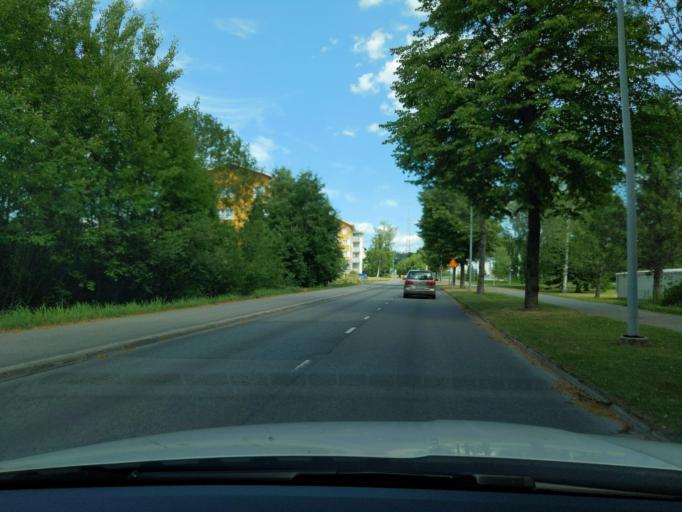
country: FI
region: Paijanne Tavastia
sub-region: Lahti
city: Lahti
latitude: 60.9701
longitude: 25.6339
